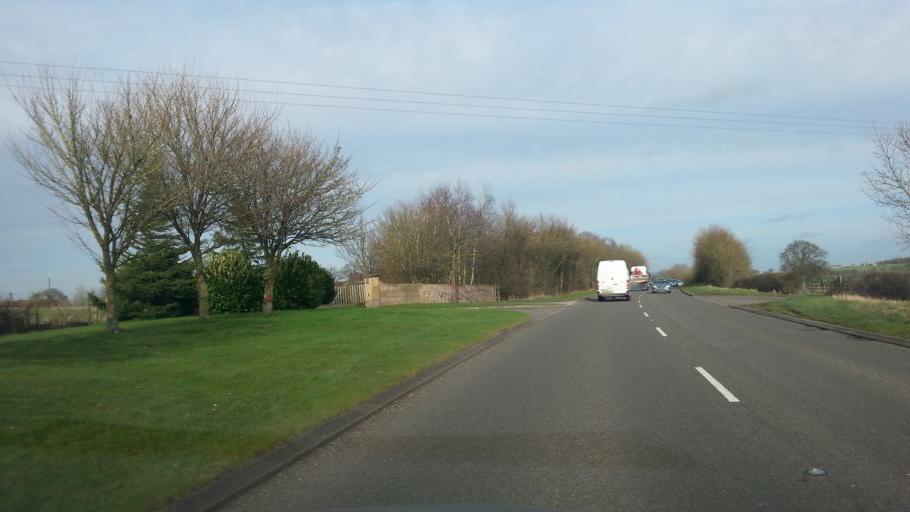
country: GB
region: England
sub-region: Staffordshire
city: Colwich
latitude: 52.8641
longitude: -1.9511
